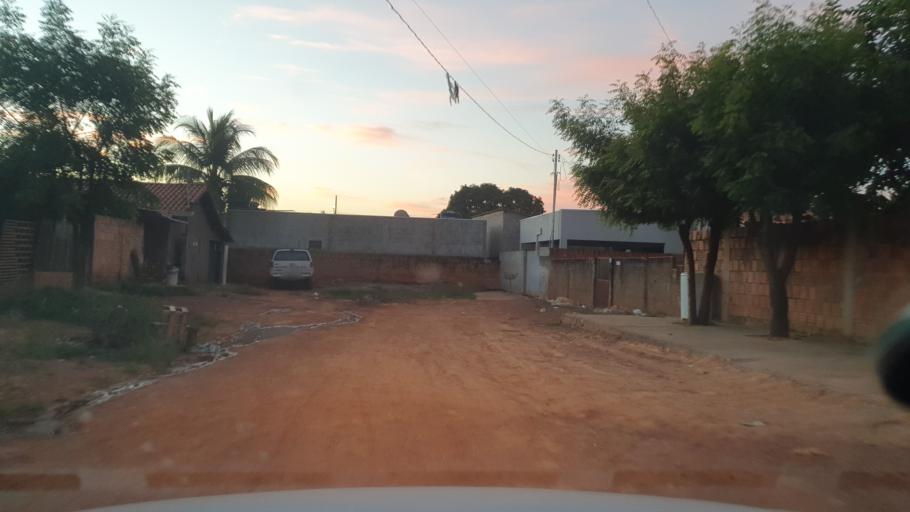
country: BR
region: Mato Grosso
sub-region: Pontes E Lacerda
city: Pontes e Lacerda
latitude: -15.2260
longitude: -59.3492
